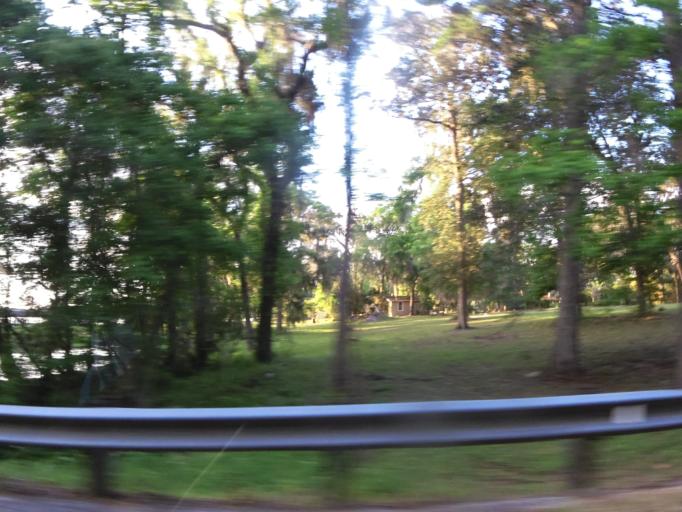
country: US
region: Florida
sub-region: Saint Johns County
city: Fruit Cove
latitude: 30.1277
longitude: -81.6035
